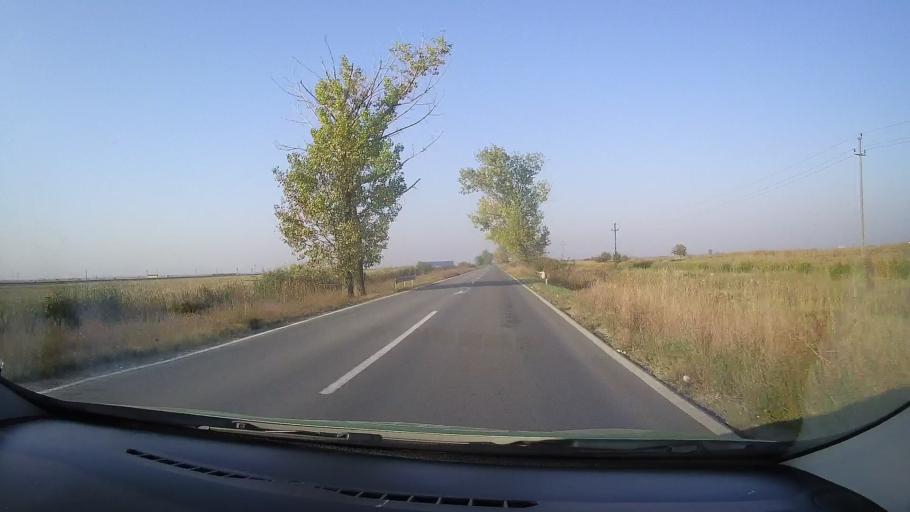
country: RO
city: Chisineu-Cris
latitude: 46.5114
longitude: 21.4835
